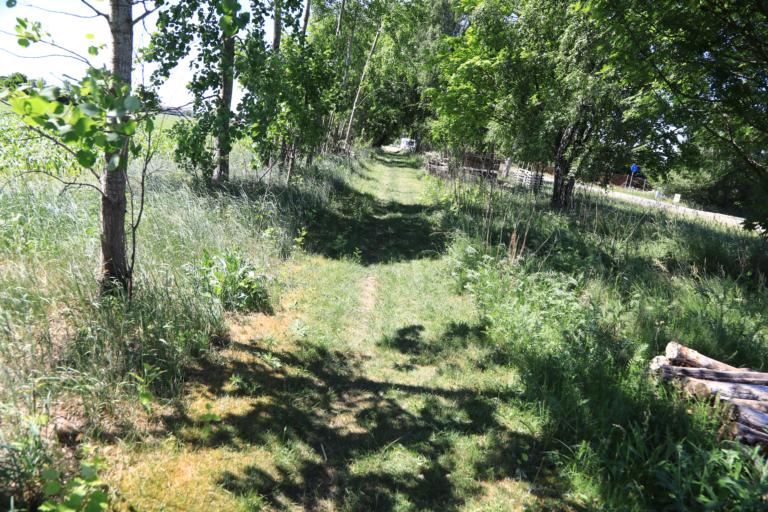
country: SE
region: Halland
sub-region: Varbergs Kommun
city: Tvaaker
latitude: 57.1009
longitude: 12.3571
